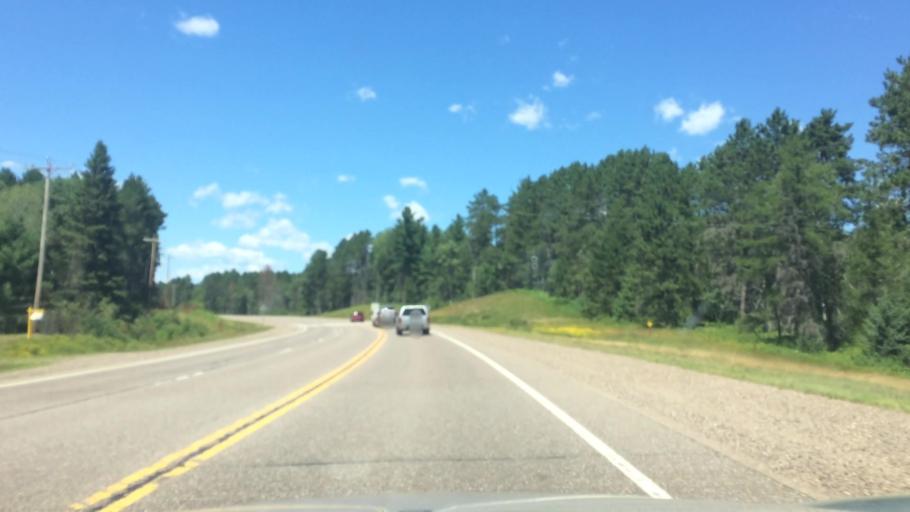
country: US
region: Wisconsin
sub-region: Lincoln County
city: Tomahawk
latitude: 45.6565
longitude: -89.7051
